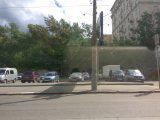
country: RU
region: Moskovskaya
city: Bogorodskoye
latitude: 55.7828
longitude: 37.7383
